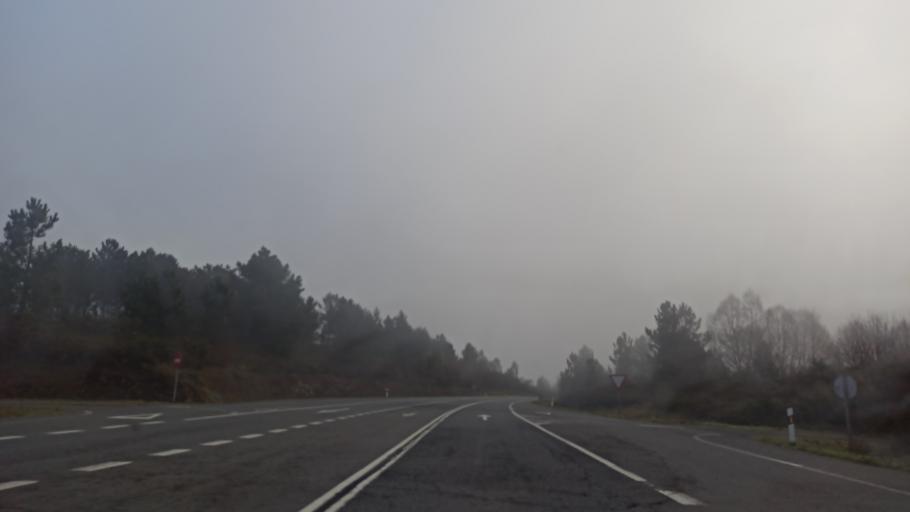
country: ES
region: Galicia
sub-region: Provincia da Coruna
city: As Pontes de Garcia Rodriguez
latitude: 43.4411
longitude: -7.8928
